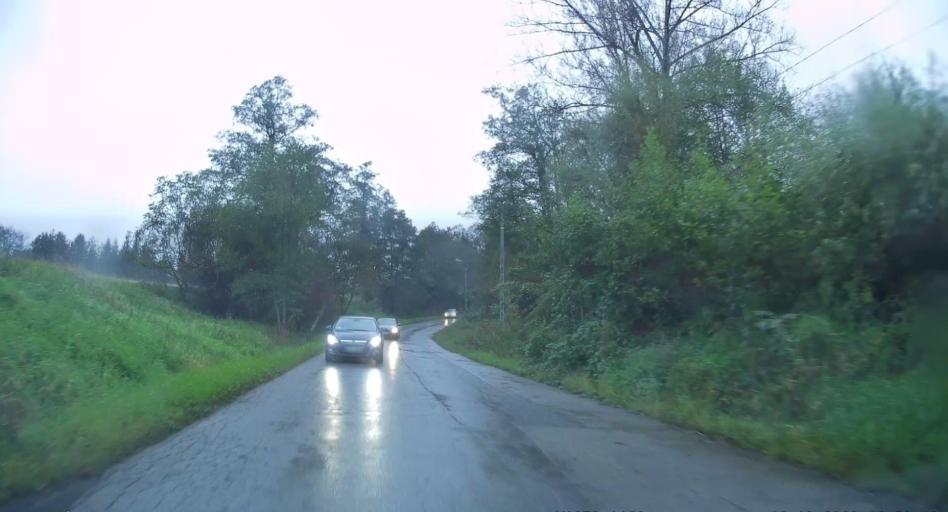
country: PL
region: Lesser Poland Voivodeship
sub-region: Powiat krakowski
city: Ochojno
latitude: 49.9694
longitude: 19.9979
